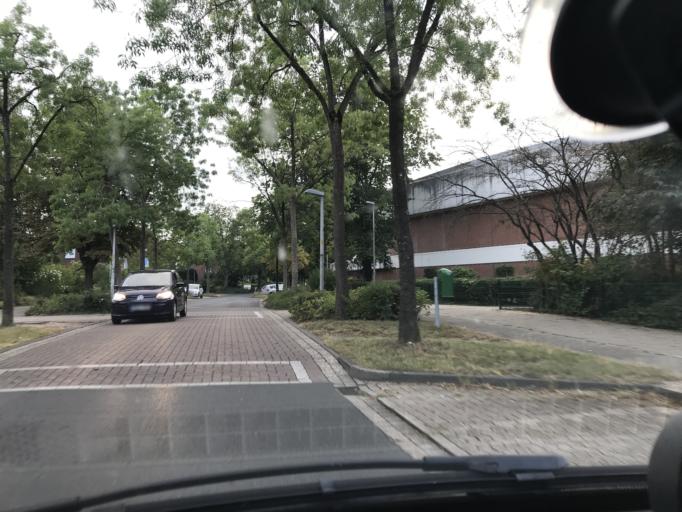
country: DE
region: Lower Saxony
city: Buxtehude
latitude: 53.4783
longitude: 9.6960
